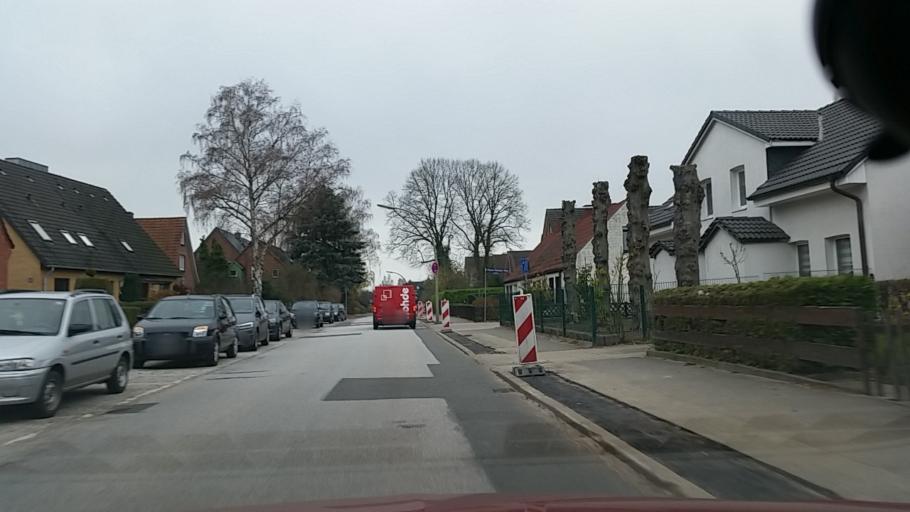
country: DE
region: Schleswig-Holstein
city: Oststeinbek
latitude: 53.5344
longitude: 10.1295
